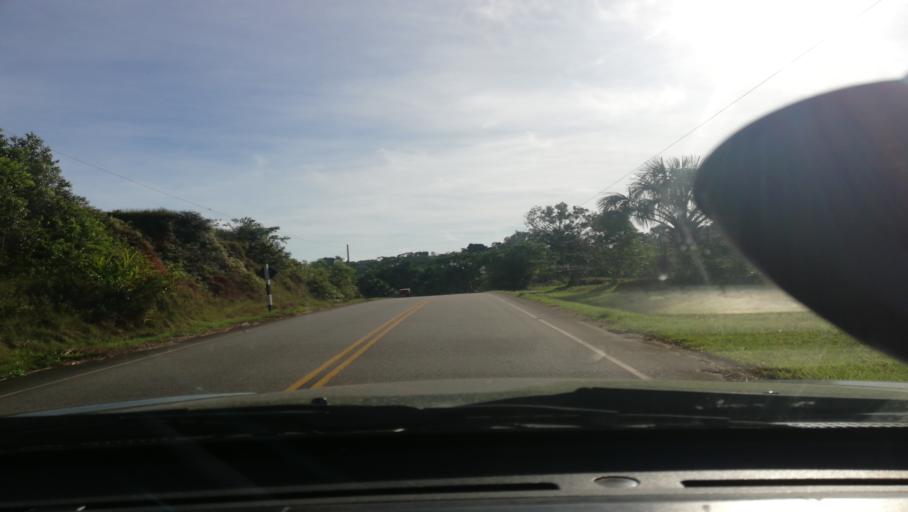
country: PE
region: Loreto
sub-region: Provincia de Loreto
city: Nauta
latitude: -4.3993
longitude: -73.5744
